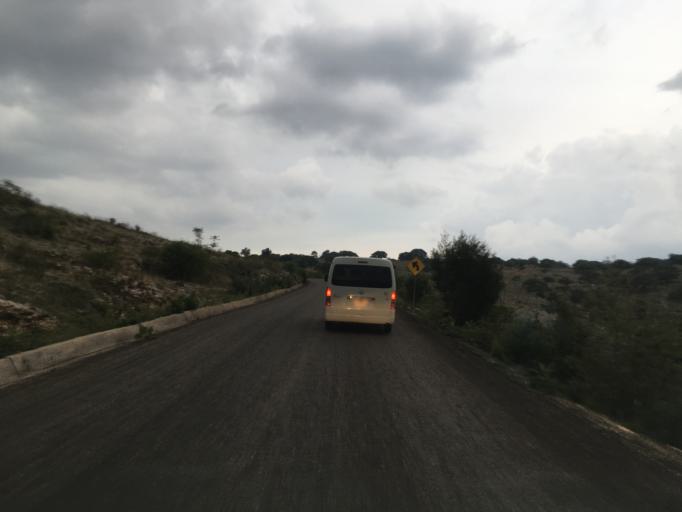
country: MX
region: Oaxaca
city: Magdalena Jaltepec
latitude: 17.2961
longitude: -97.2721
